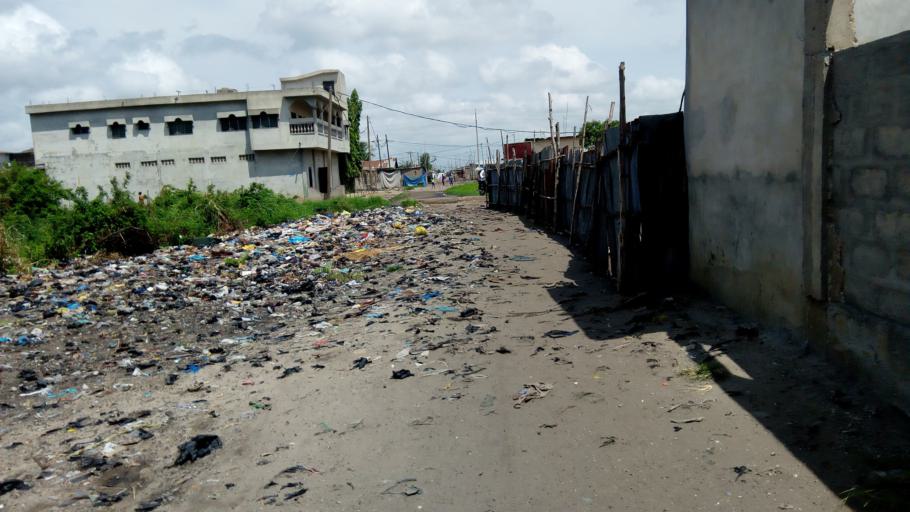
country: BJ
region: Littoral
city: Cotonou
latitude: 6.3873
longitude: 2.4332
